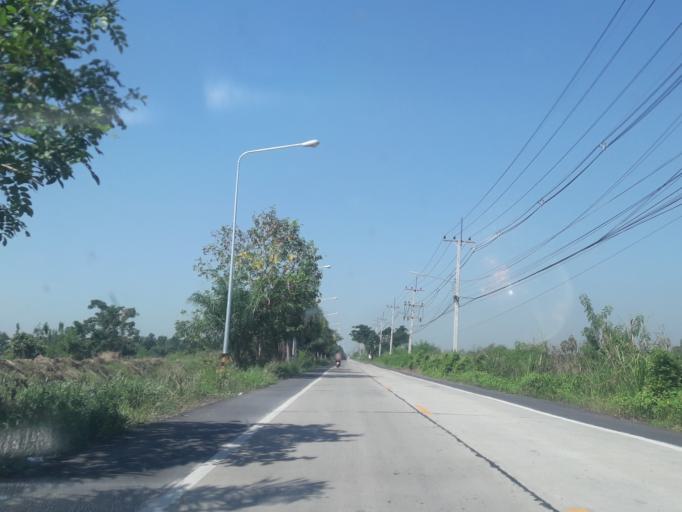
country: TH
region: Pathum Thani
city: Nong Suea
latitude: 14.1363
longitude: 100.8604
